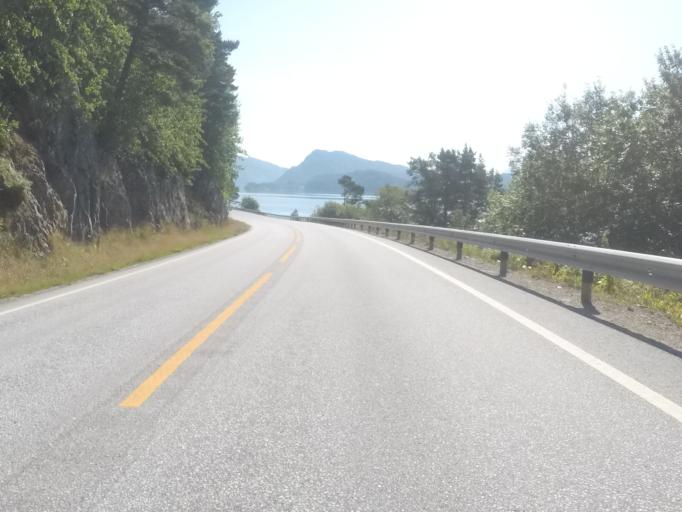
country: NO
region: Sogn og Fjordane
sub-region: Flora
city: Floro
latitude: 61.6017
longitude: 5.1485
